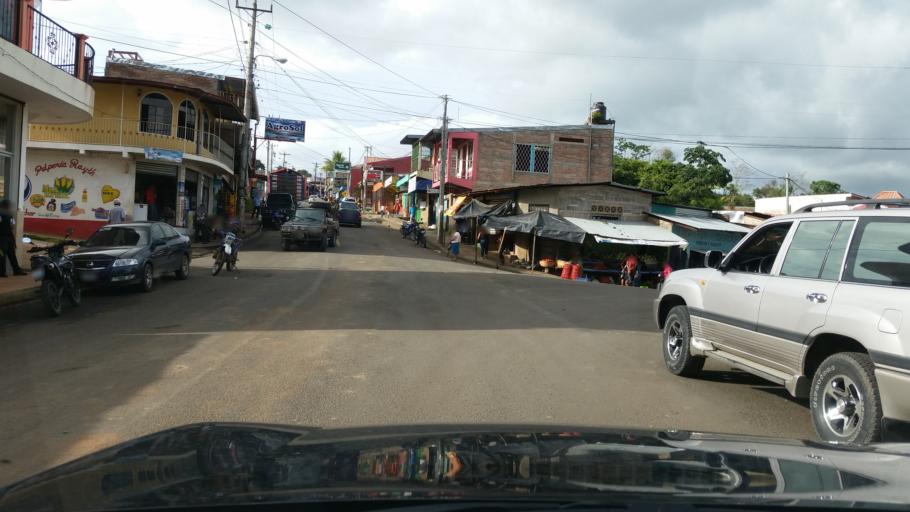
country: NI
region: Matagalpa
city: San Ramon
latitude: 13.1371
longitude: -85.7361
